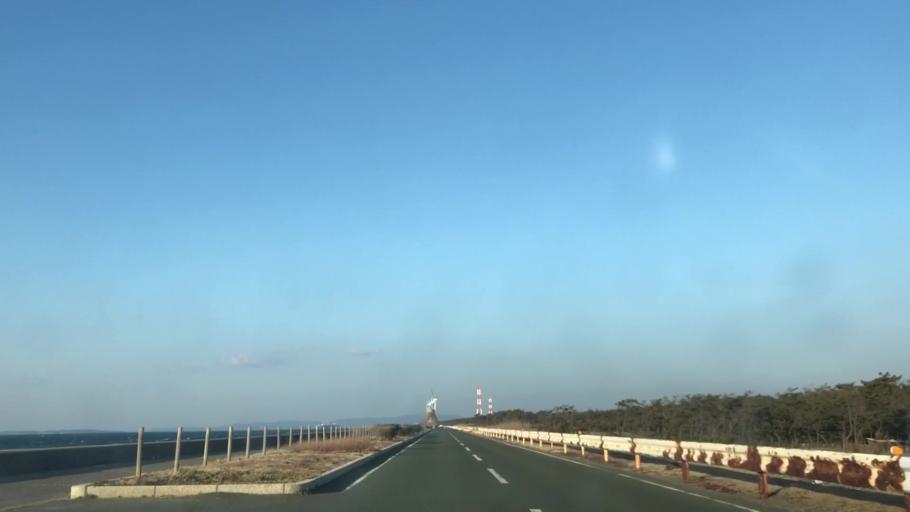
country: JP
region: Aichi
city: Toyohama
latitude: 34.6198
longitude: 137.0420
